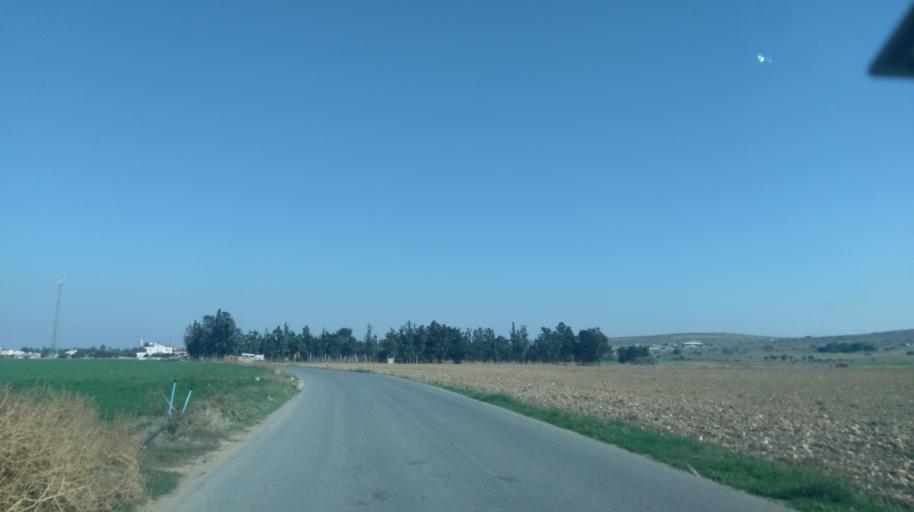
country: CY
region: Larnaka
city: Troulloi
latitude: 35.0869
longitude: 33.6193
